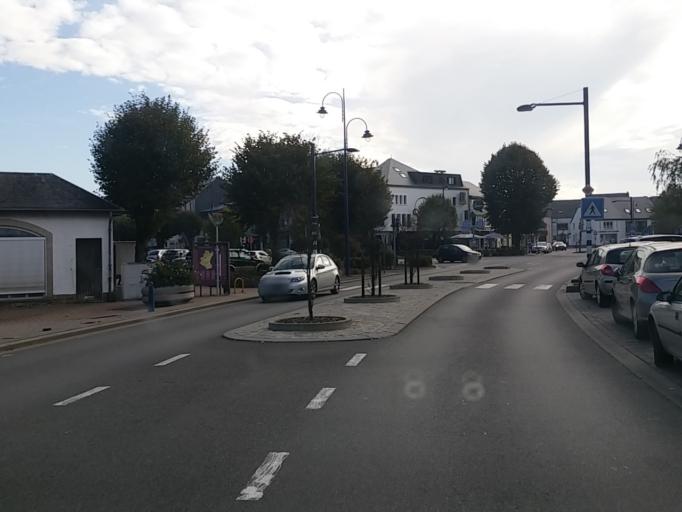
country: BE
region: Wallonia
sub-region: Province du Luxembourg
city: Florenville
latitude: 49.6980
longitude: 5.3106
